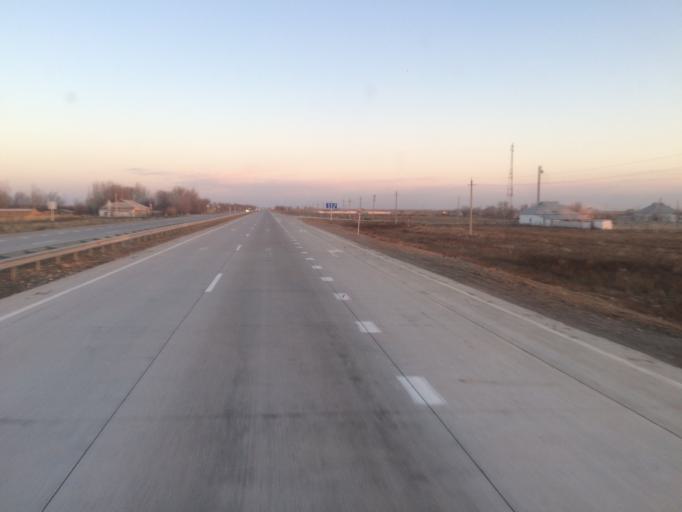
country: KZ
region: Ongtustik Qazaqstan
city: Bayaldyr
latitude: 43.0620
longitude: 68.6811
